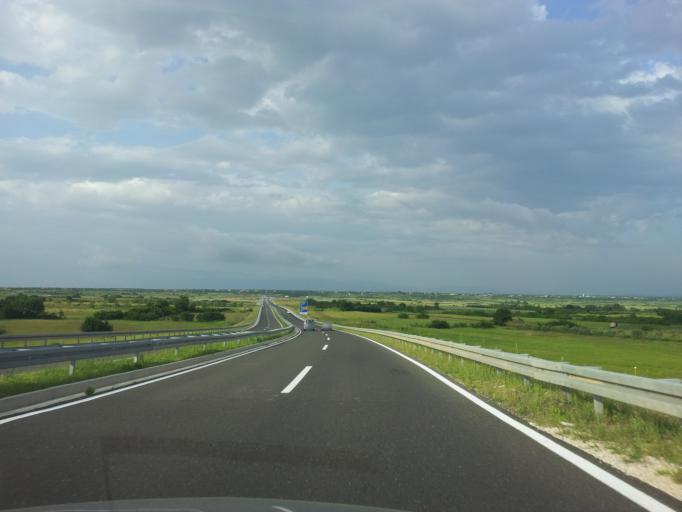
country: HR
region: Zadarska
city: Galovac
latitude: 44.1013
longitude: 15.3886
